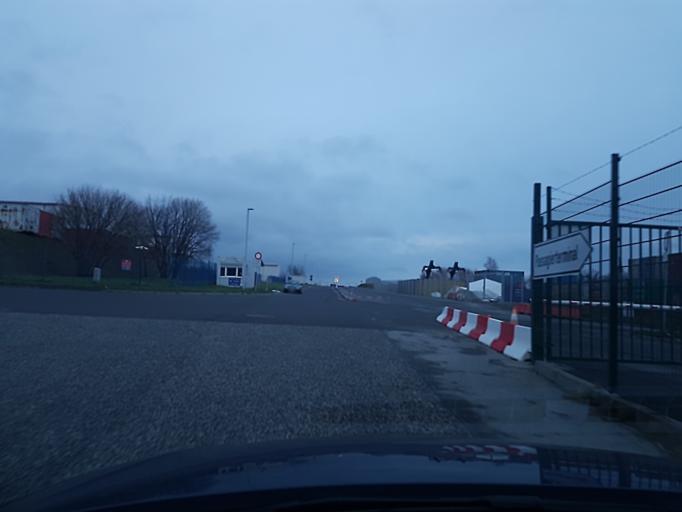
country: DE
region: Mecklenburg-Vorpommern
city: Sagard
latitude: 54.4867
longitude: 13.5901
